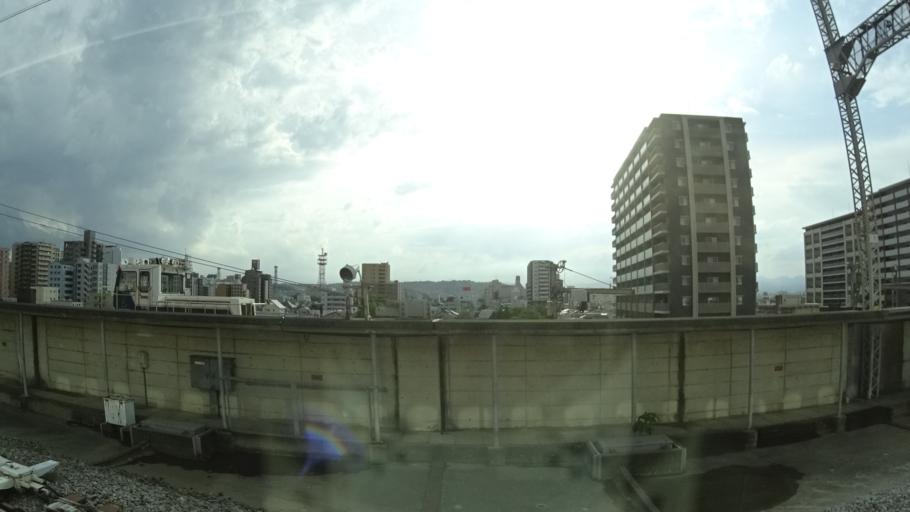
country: JP
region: Gunma
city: Takasaki
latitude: 36.3295
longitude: 139.0122
